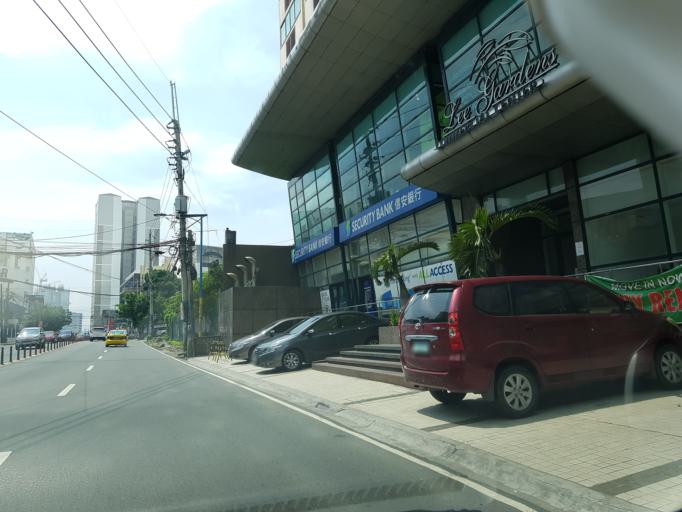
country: PH
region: Metro Manila
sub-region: Mandaluyong
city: Mandaluyong City
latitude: 14.5874
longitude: 121.0462
